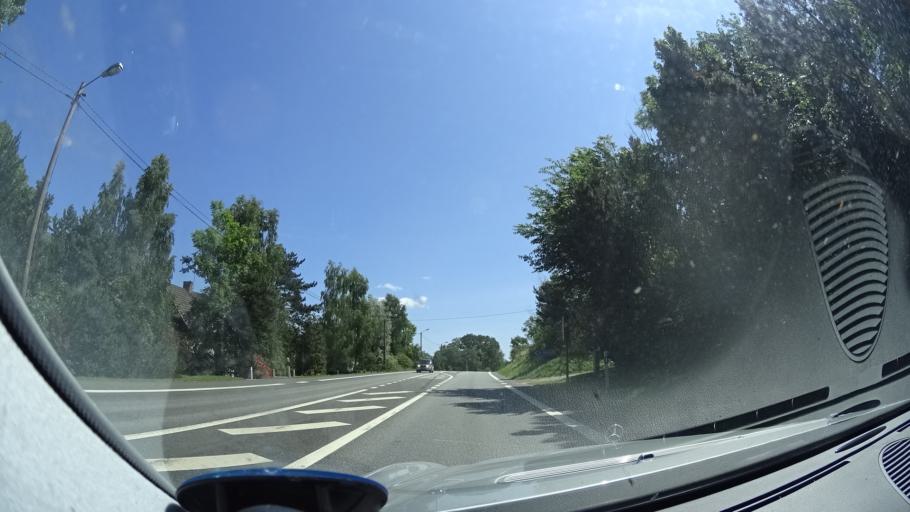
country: SE
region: Skane
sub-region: Hassleholms Kommun
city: Vinslov
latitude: 55.9434
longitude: 13.8995
